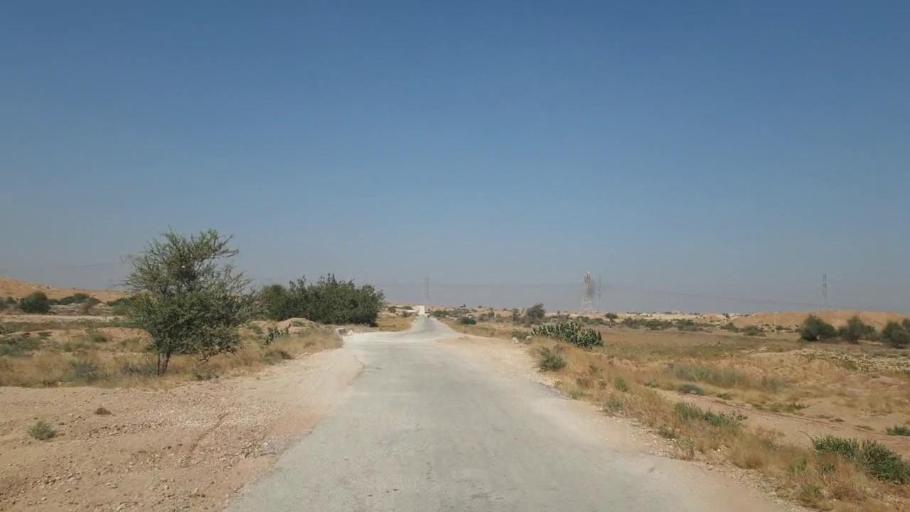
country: PK
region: Sindh
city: Thatta
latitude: 25.1932
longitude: 67.8015
